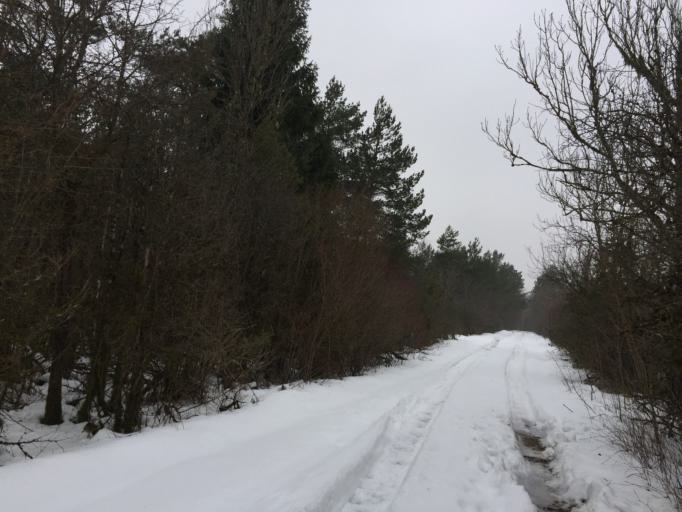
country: EE
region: Saare
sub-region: Orissaare vald
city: Orissaare
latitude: 58.4206
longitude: 22.8195
